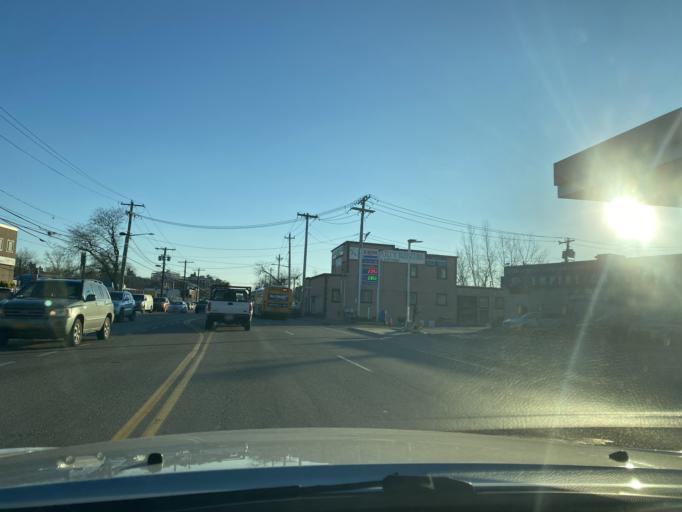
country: US
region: New York
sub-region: Nassau County
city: Inwood
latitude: 40.6143
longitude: -73.7527
